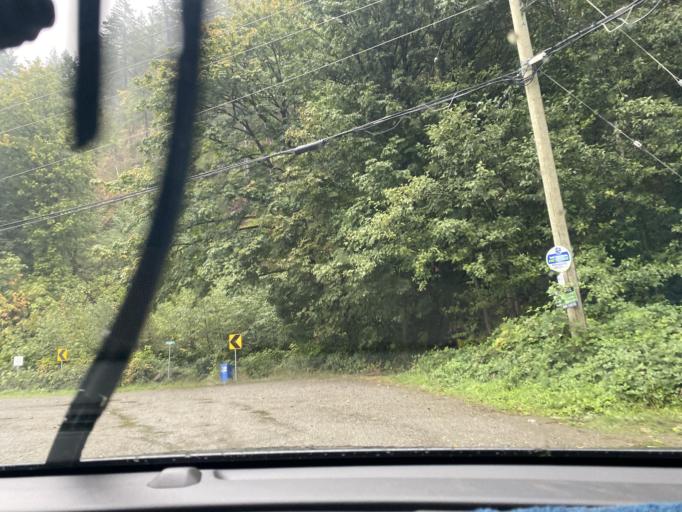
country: CA
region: British Columbia
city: Agassiz
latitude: 49.3038
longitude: -121.7732
